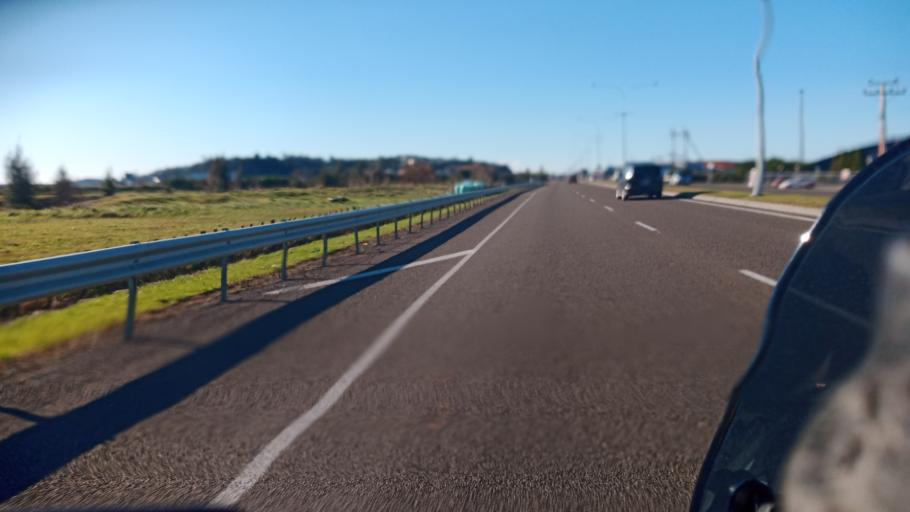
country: NZ
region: Hawke's Bay
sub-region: Napier City
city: Napier
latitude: -39.4963
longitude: 176.8766
